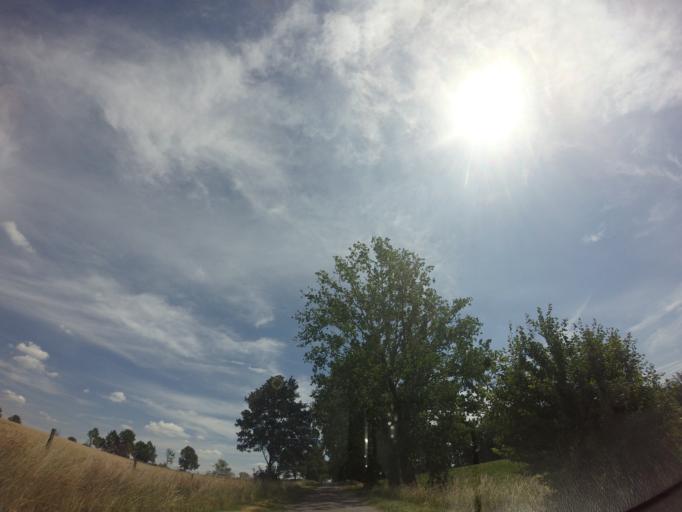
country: PL
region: West Pomeranian Voivodeship
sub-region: Powiat choszczenski
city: Recz
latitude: 53.3455
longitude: 15.5506
